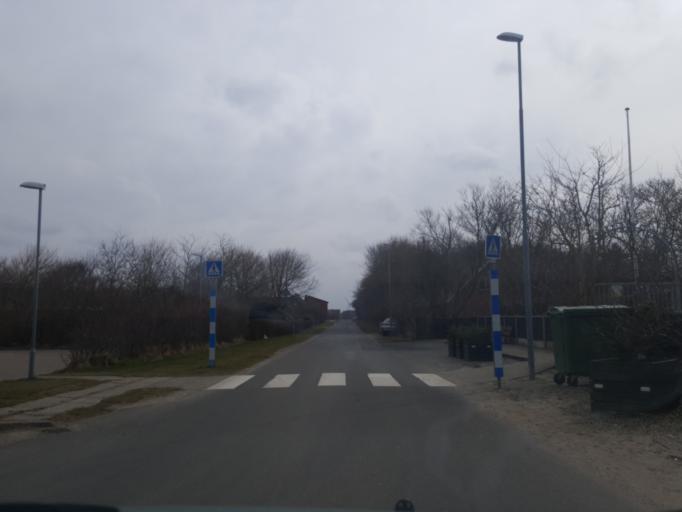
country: DK
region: Central Jutland
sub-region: Ringkobing-Skjern Kommune
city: Ringkobing
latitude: 56.2000
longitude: 8.2059
